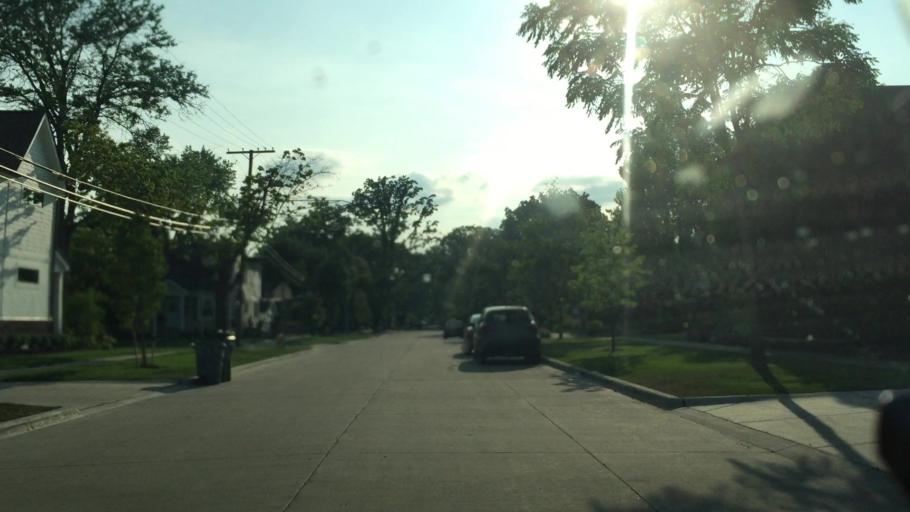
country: US
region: Michigan
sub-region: Oakland County
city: Beverly Hills
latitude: 42.5340
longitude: -83.2150
